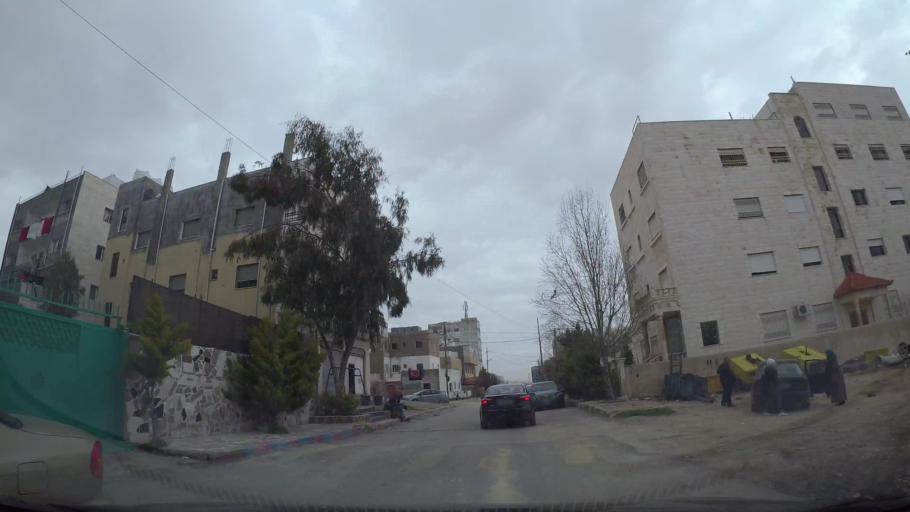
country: JO
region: Amman
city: Wadi as Sir
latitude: 31.9425
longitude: 35.8308
